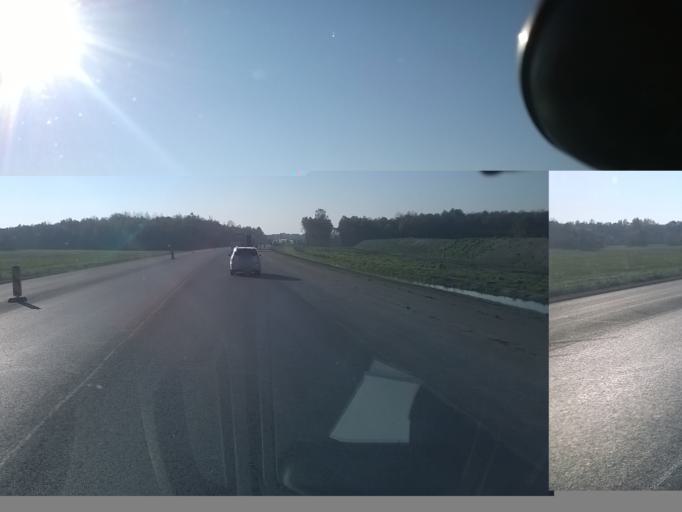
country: EE
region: Harju
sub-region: Rae vald
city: Jueri
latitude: 59.3819
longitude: 24.9184
